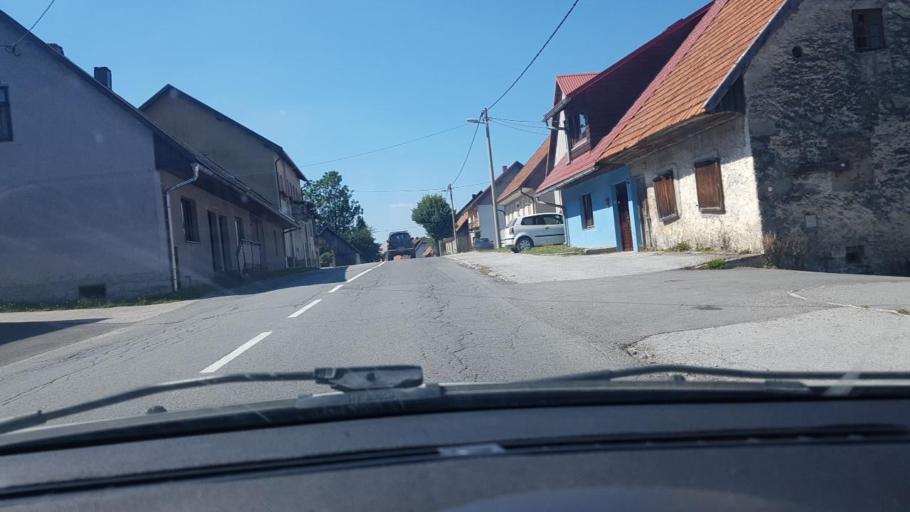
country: HR
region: Primorsko-Goranska
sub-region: Grad Delnice
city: Delnice
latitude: 45.3734
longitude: 14.9305
